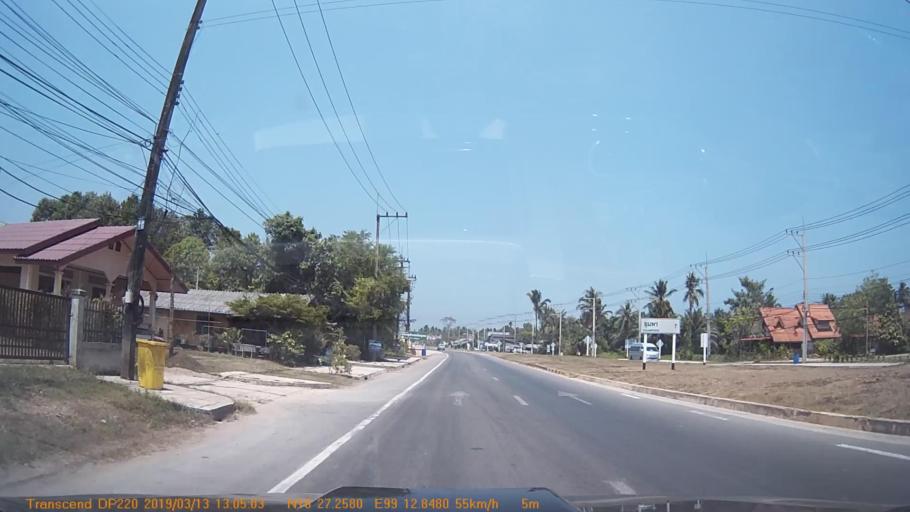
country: TH
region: Chumphon
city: Chumphon
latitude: 10.4546
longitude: 99.2142
